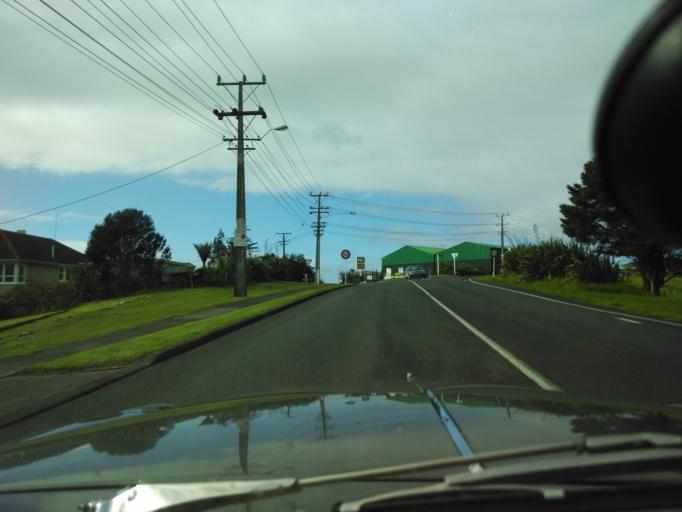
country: NZ
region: Auckland
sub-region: Auckland
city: Wellsford
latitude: -36.2986
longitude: 174.5192
